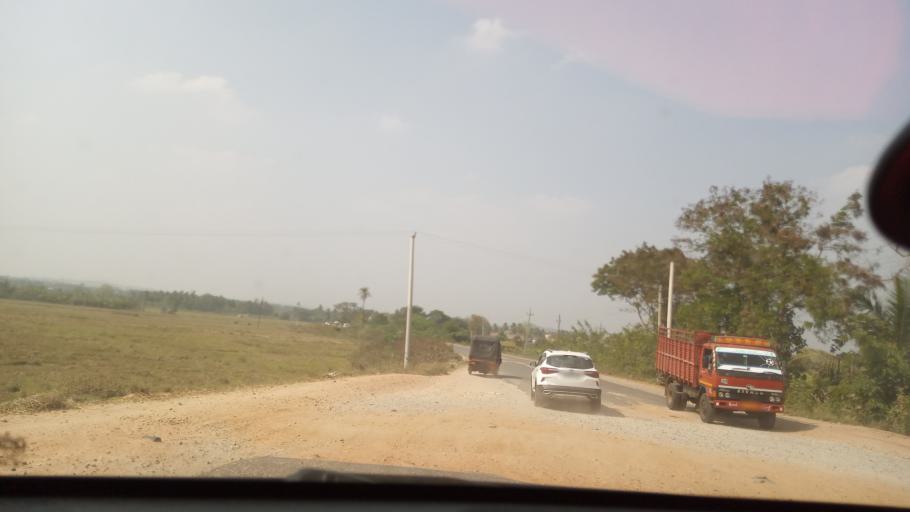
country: IN
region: Karnataka
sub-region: Mysore
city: Nanjangud
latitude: 12.1074
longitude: 76.7067
